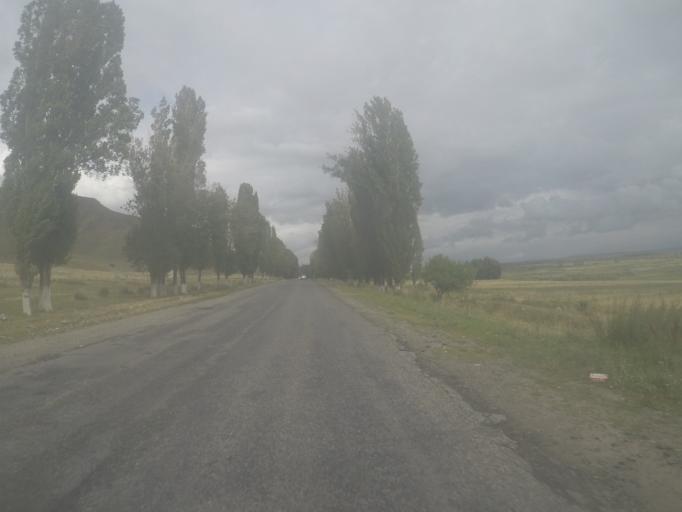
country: KG
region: Ysyk-Koel
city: Tyup
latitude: 42.7432
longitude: 78.0416
